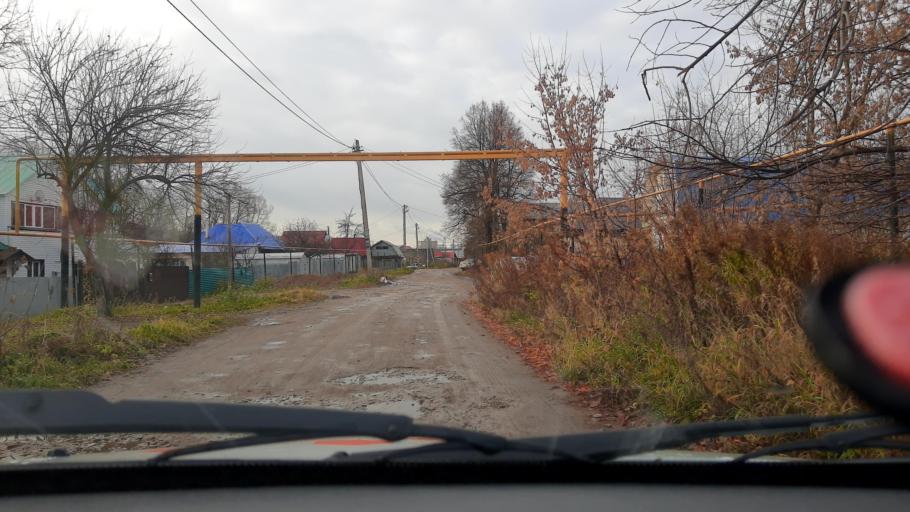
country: RU
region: Bashkortostan
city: Ufa
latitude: 54.8296
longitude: 56.1325
